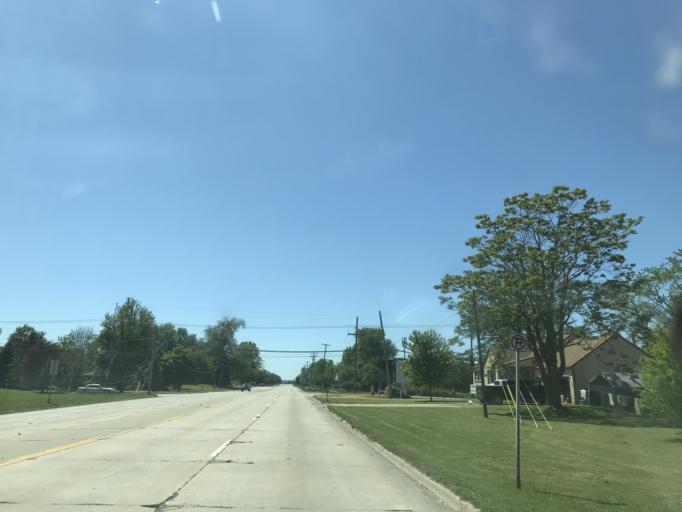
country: US
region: Michigan
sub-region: Wayne County
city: Taylor
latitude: 42.2102
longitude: -83.3156
